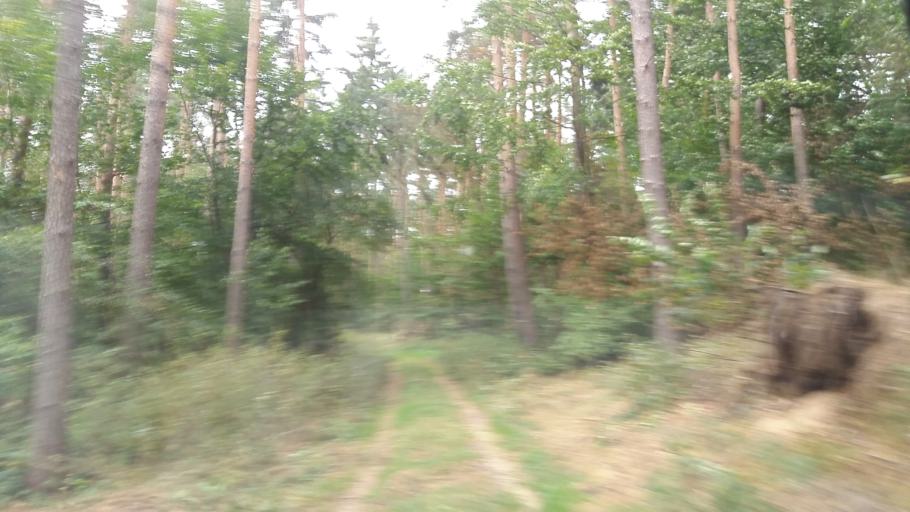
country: PL
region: West Pomeranian Voivodeship
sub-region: Powiat choszczenski
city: Bierzwnik
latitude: 52.9902
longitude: 15.6074
